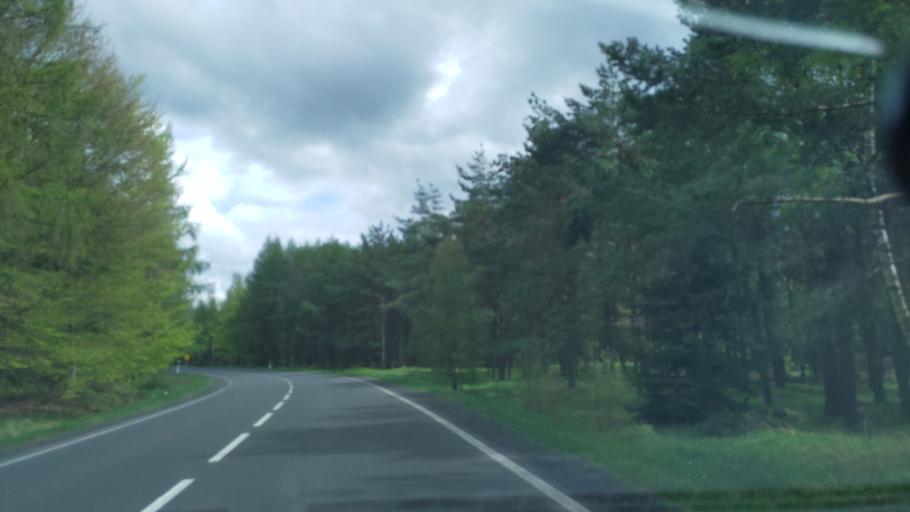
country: CZ
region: Ustecky
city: Libouchec
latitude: 50.7850
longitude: 14.0475
